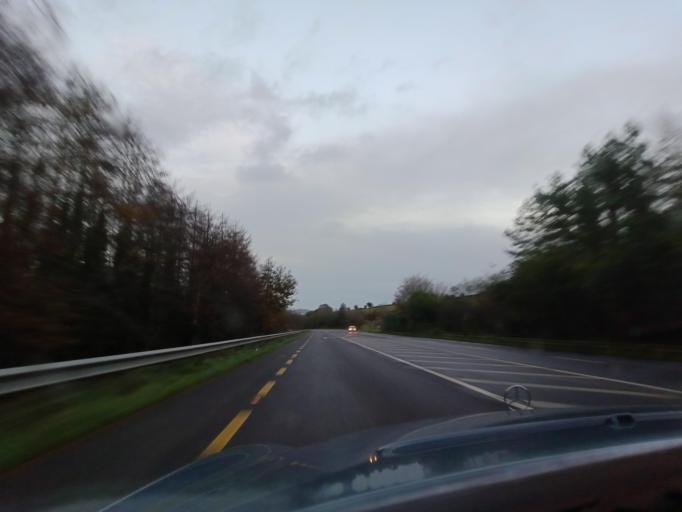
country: IE
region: Munster
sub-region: Waterford
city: Waterford
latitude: 52.3473
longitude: -7.0426
